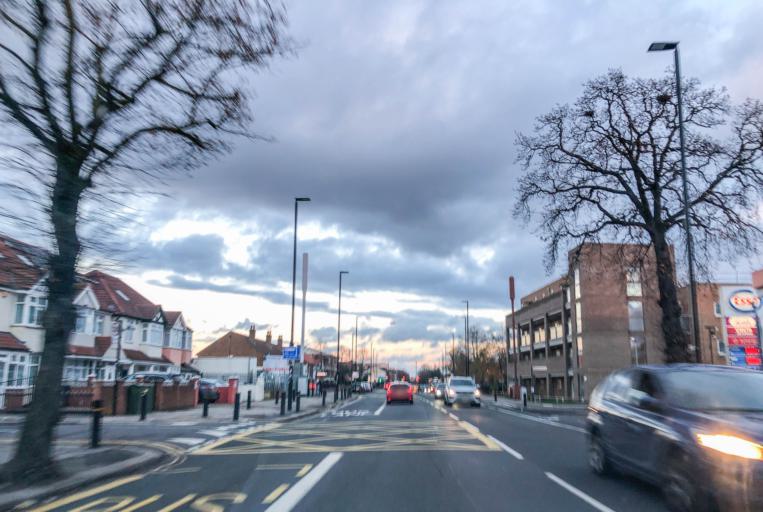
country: GB
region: England
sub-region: Greater London
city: Hounslow
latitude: 51.4645
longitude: -0.3816
